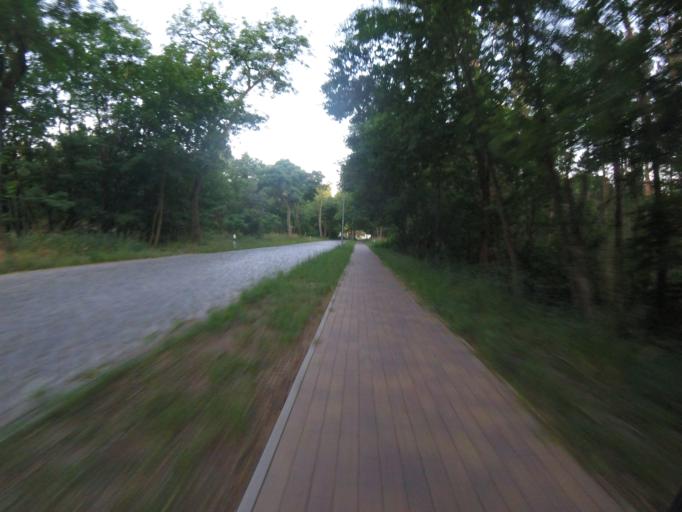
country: DE
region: Brandenburg
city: Konigs Wusterhausen
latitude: 52.2716
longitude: 13.6016
